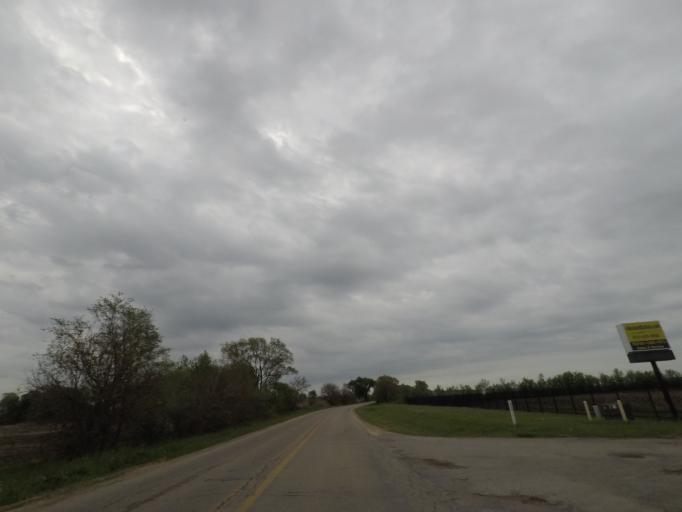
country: US
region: Illinois
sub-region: Winnebago County
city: Roscoe
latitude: 42.4505
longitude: -88.9909
